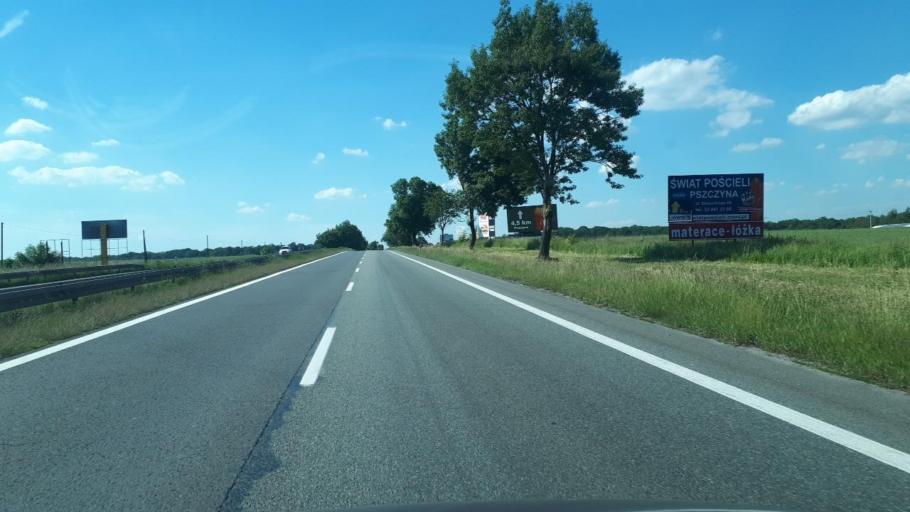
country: PL
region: Silesian Voivodeship
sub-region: Powiat pszczynski
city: Goczalkowice Zdroj
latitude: 49.9500
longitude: 18.9700
